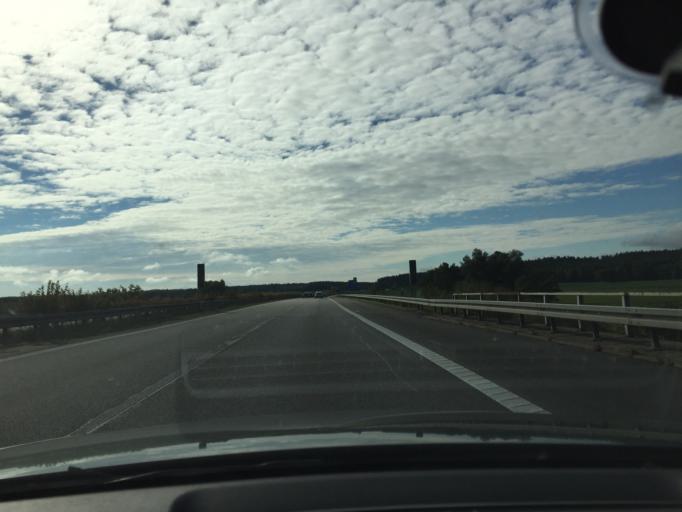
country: DE
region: Mecklenburg-Vorpommern
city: Robel
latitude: 53.3075
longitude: 12.4763
